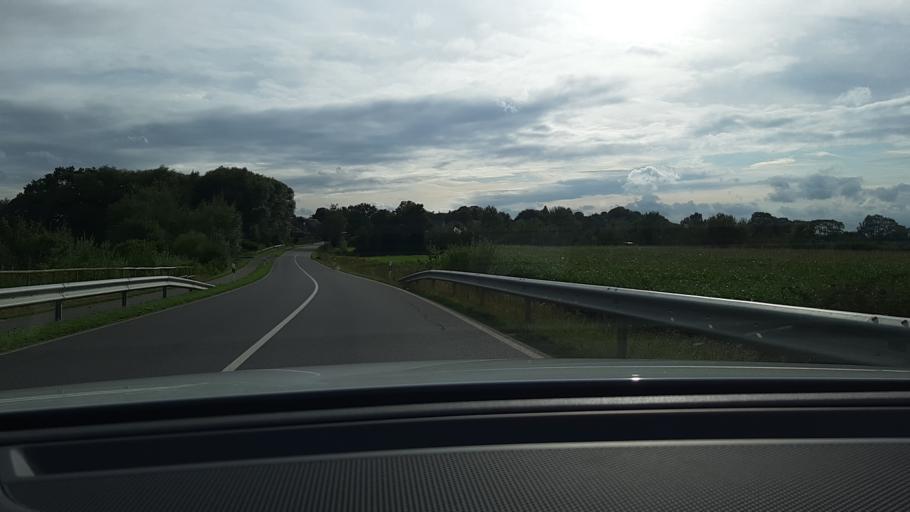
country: DE
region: Schleswig-Holstein
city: Badendorf
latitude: 53.8630
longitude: 10.5645
